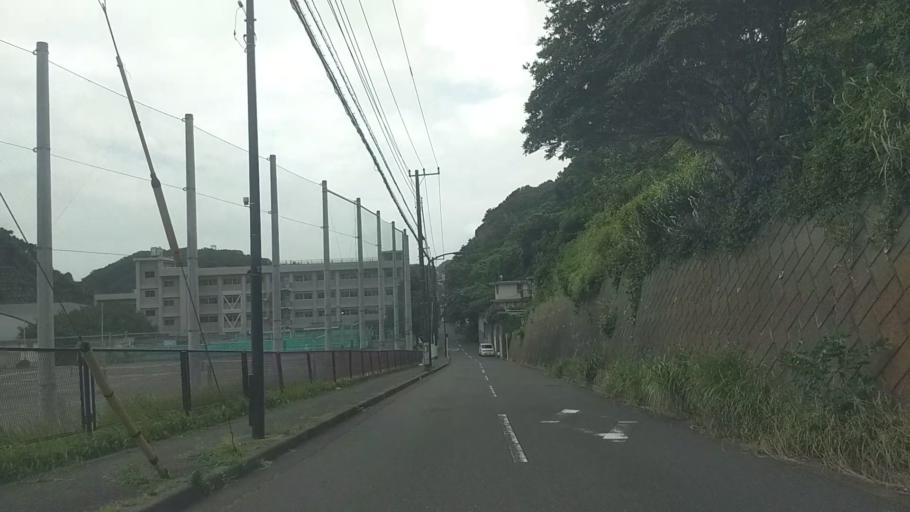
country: JP
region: Kanagawa
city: Yokosuka
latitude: 35.2540
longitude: 139.7337
